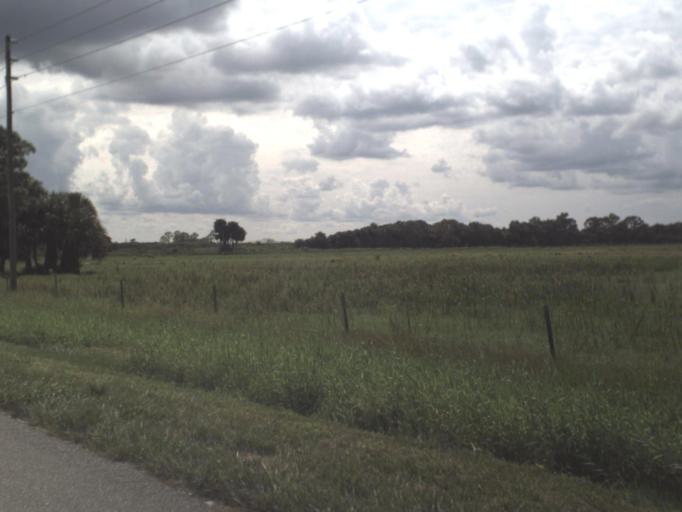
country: US
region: Florida
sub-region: DeSoto County
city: Nocatee
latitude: 27.0112
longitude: -81.7604
